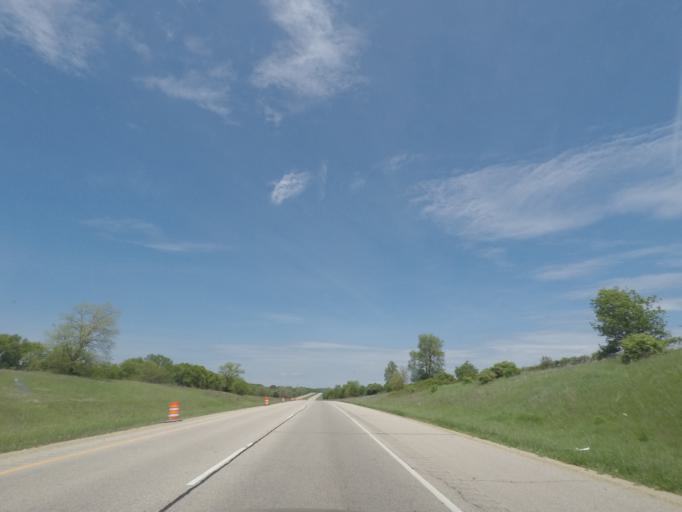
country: US
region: Wisconsin
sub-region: Dane County
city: Oregon
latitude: 42.9771
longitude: -89.3856
